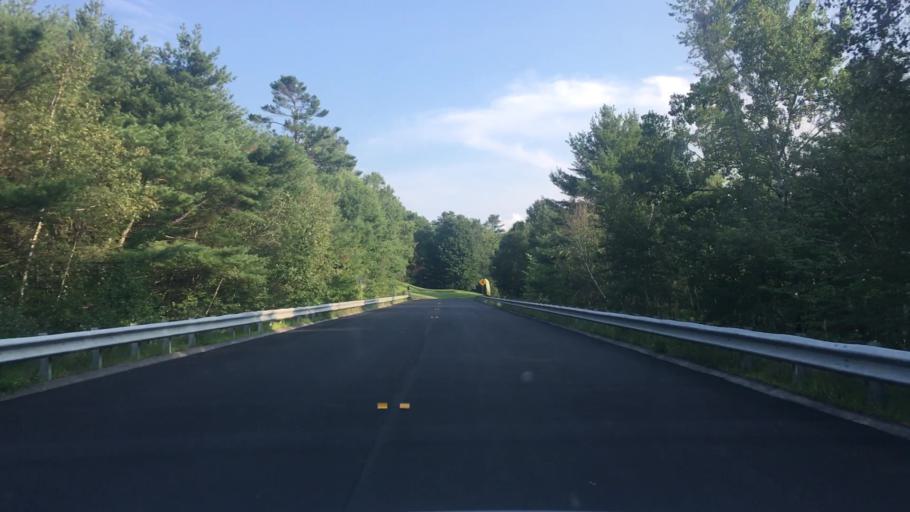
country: US
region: New Hampshire
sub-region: Sullivan County
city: Grantham
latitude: 43.5036
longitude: -72.1315
